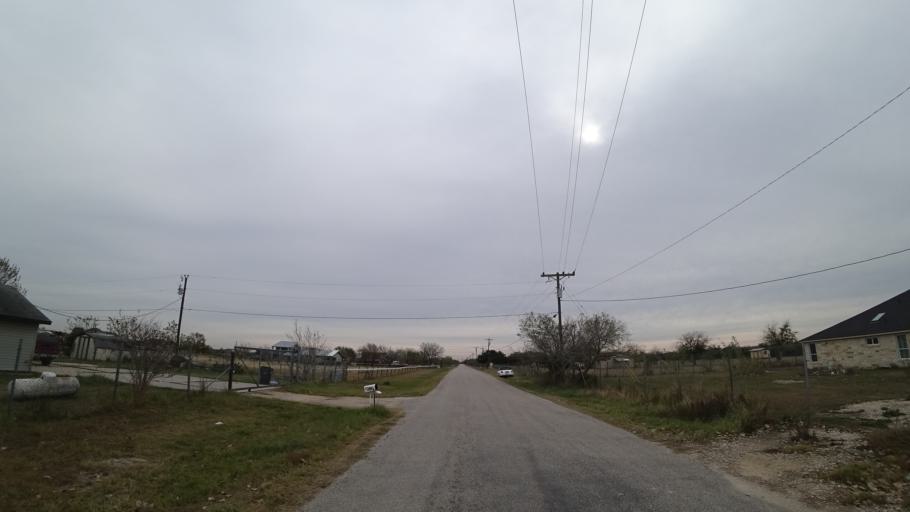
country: US
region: Texas
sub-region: Travis County
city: Garfield
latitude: 30.1129
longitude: -97.5814
